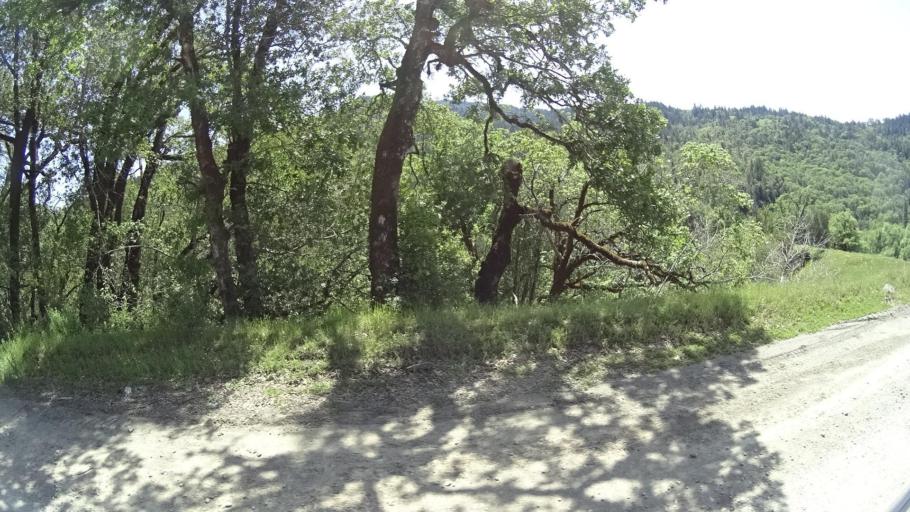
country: US
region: California
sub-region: Humboldt County
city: Redway
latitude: 40.1933
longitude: -123.5641
